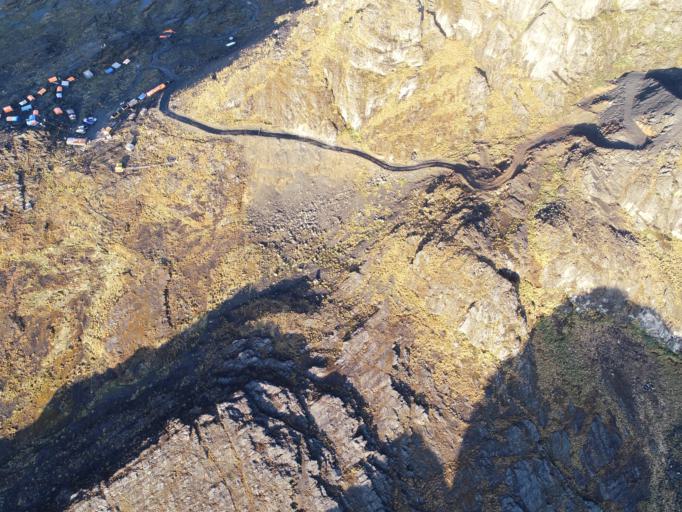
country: PE
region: Puno
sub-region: San Antonio De Putina
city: Sina
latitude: -14.7378
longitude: -69.0478
